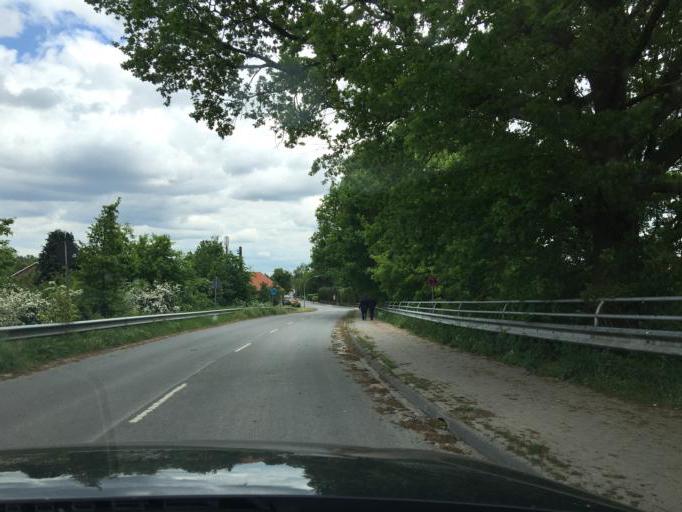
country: DE
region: North Rhine-Westphalia
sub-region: Regierungsbezirk Munster
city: Muenster
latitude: 52.0346
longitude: 7.6722
